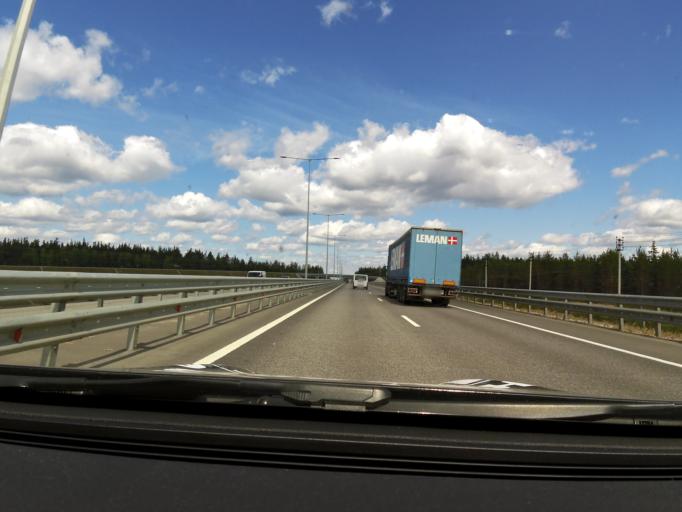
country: RU
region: Tverskaya
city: Krasnomayskiy
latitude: 57.5527
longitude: 34.2686
